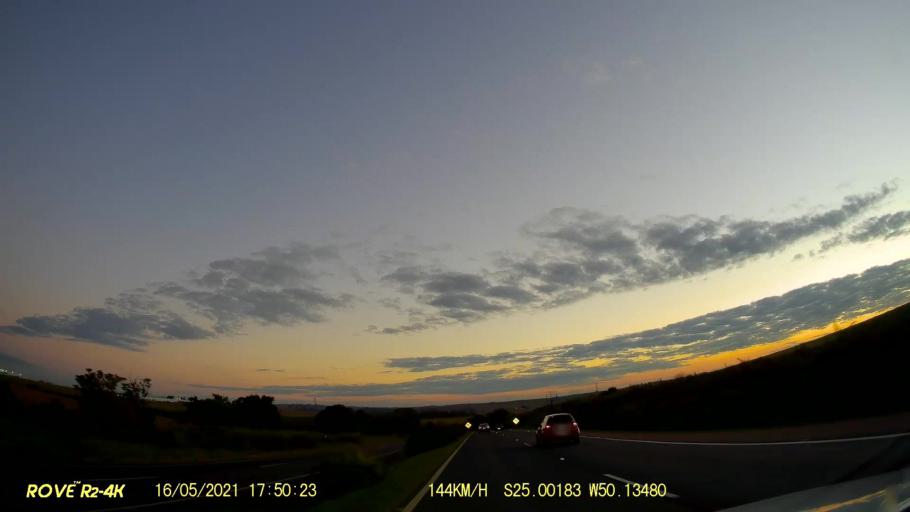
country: BR
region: Parana
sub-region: Carambei
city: Carambei
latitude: -25.0019
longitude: -50.1349
